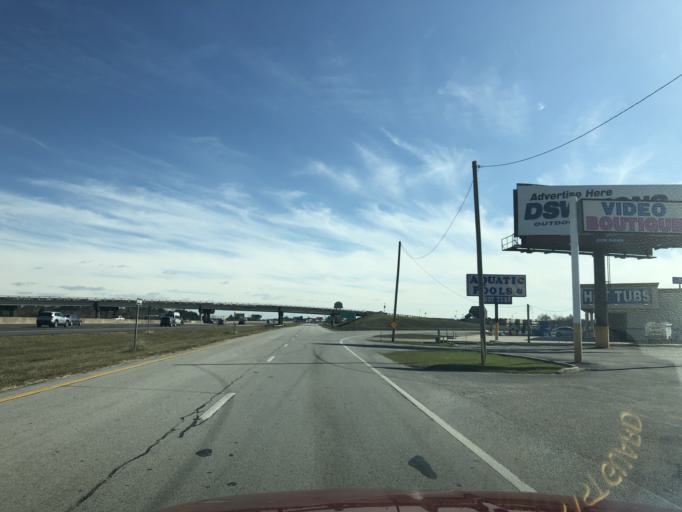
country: US
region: Texas
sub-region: Galveston County
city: Hitchcock
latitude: 29.3913
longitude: -95.0222
